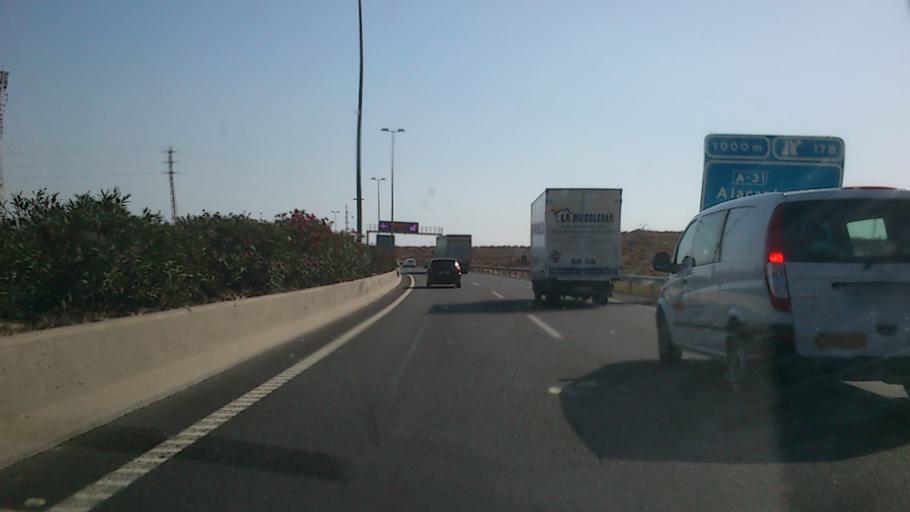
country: ES
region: Valencia
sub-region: Provincia de Alicante
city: San Vicent del Raspeig
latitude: 38.3490
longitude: -0.5406
